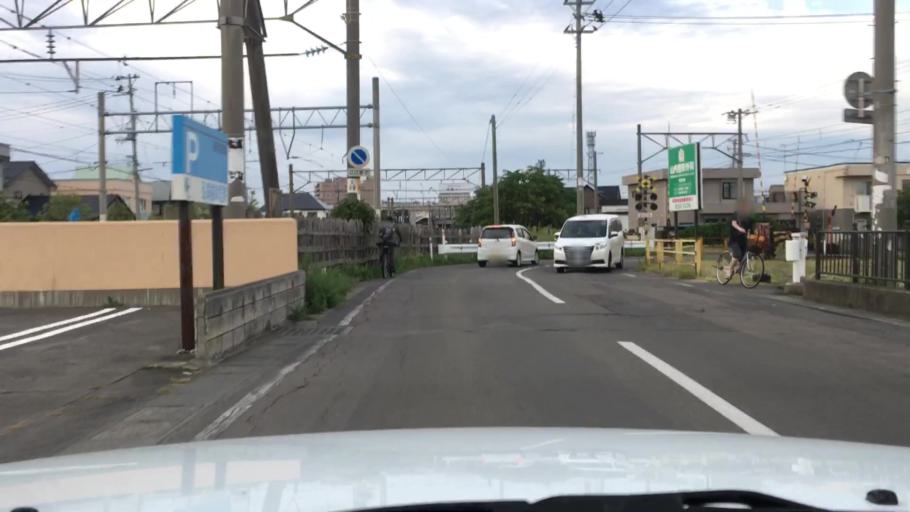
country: JP
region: Aomori
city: Hirosaki
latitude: 40.5926
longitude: 140.4878
